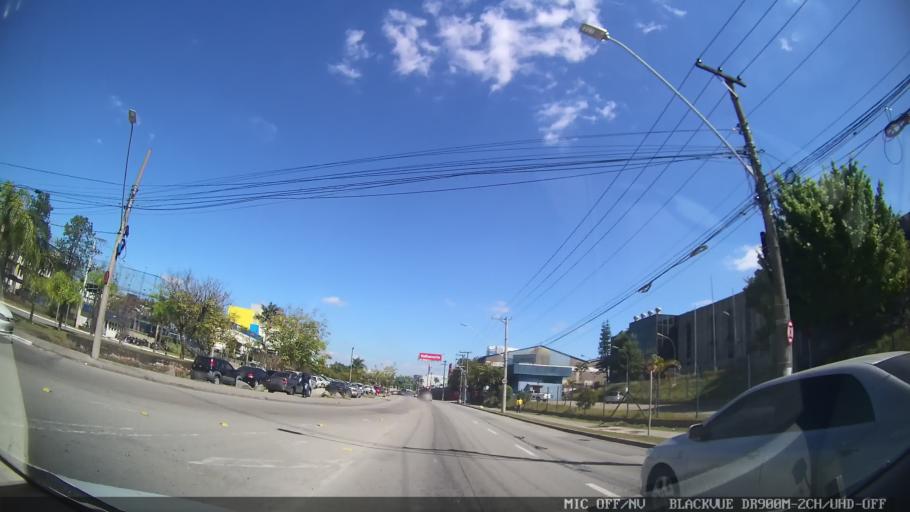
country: BR
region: Sao Paulo
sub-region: Carapicuiba
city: Carapicuiba
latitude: -23.5008
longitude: -46.8319
